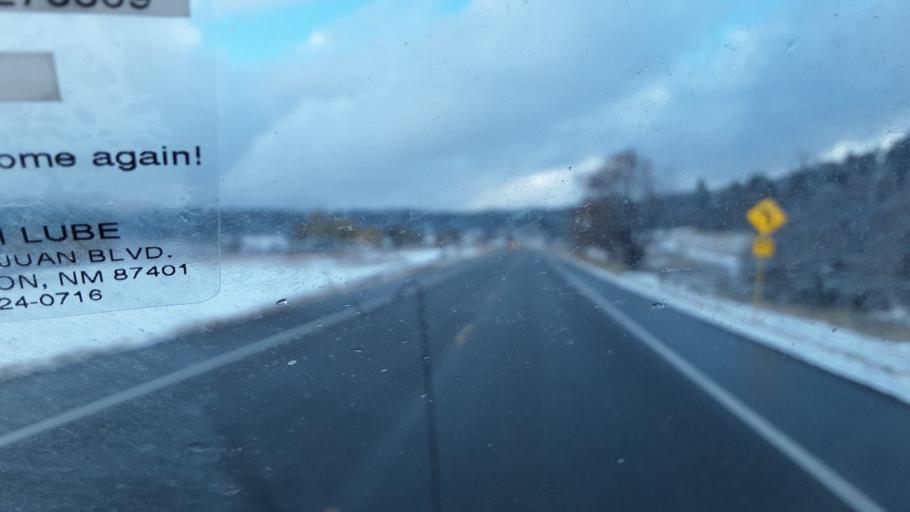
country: US
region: Colorado
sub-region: La Plata County
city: Bayfield
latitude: 37.2229
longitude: -107.6553
